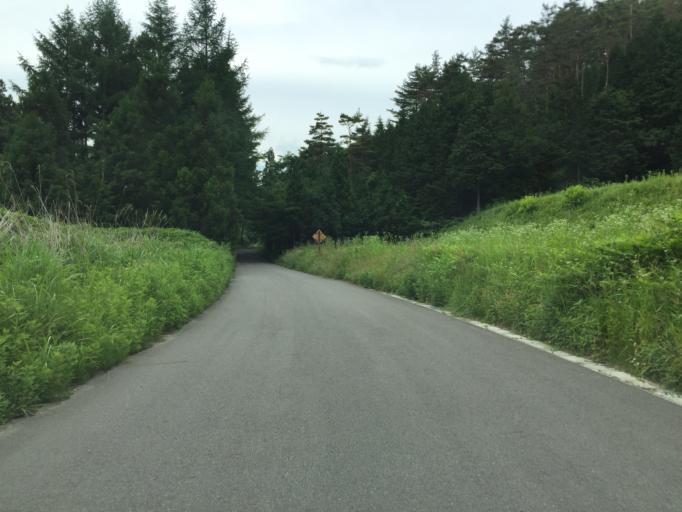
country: JP
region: Fukushima
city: Funehikimachi-funehiki
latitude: 37.4366
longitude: 140.7854
